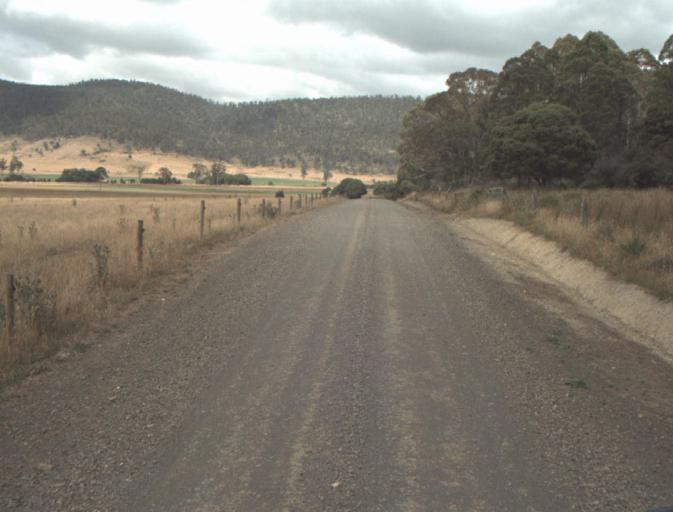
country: AU
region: Tasmania
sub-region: Northern Midlands
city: Evandale
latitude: -41.4738
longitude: 147.4459
